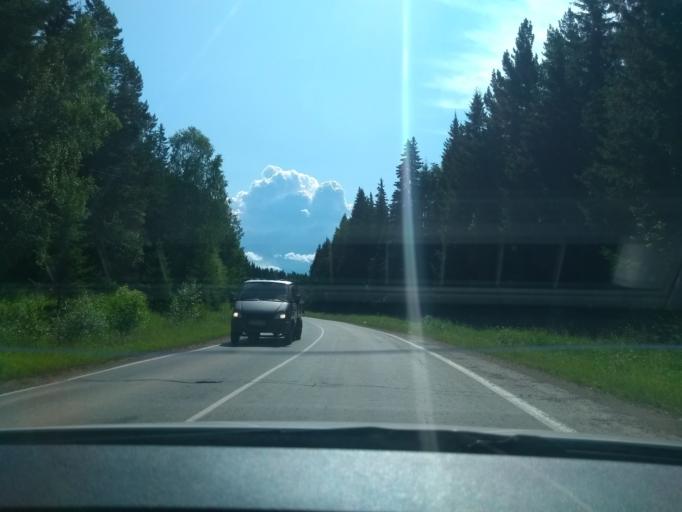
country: RU
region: Perm
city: Bershet'
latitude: 57.8283
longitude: 56.4106
